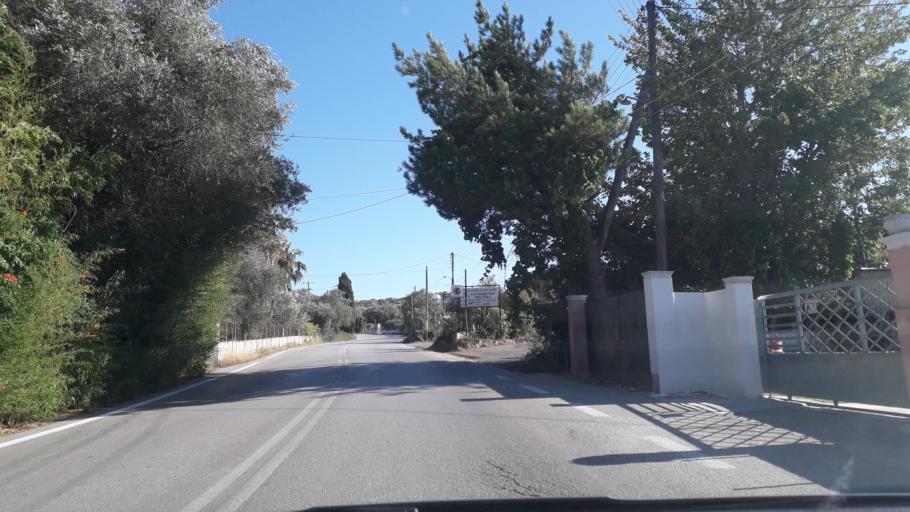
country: GR
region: Ionian Islands
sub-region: Nomos Kerkyras
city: Agios Matthaios
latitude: 39.4728
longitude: 19.9114
